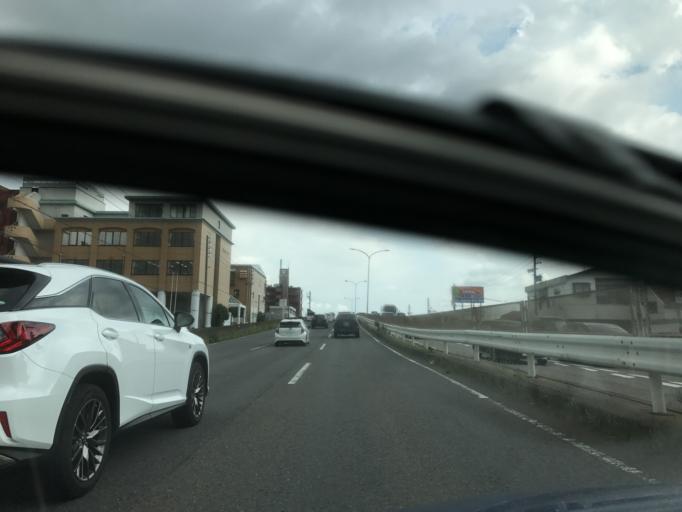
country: JP
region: Gifu
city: Gifu-shi
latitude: 35.4068
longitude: 136.7848
